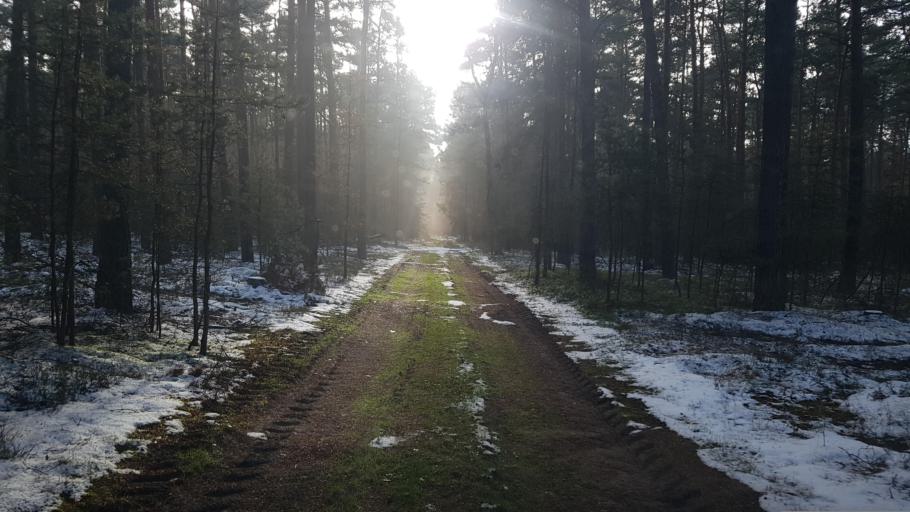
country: DE
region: Brandenburg
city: Bronkow
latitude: 51.6632
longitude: 13.8967
